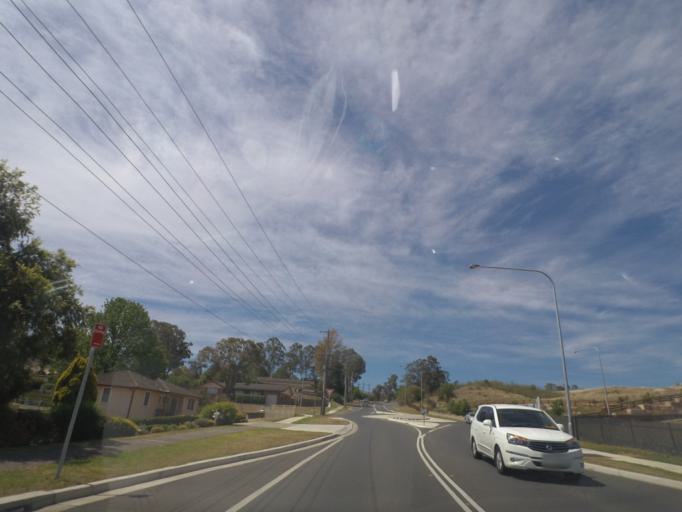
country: AU
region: New South Wales
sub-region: Wollondilly
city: Picton
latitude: -34.1647
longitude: 150.6141
